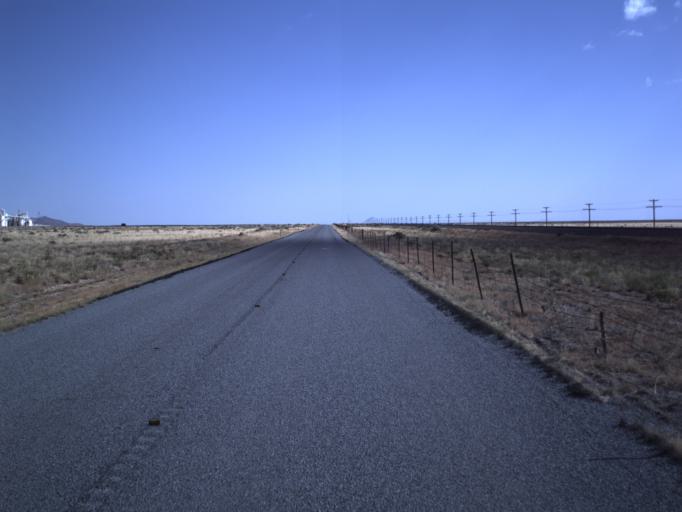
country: US
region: Utah
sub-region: Millard County
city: Fillmore
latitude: 38.9211
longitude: -112.8117
